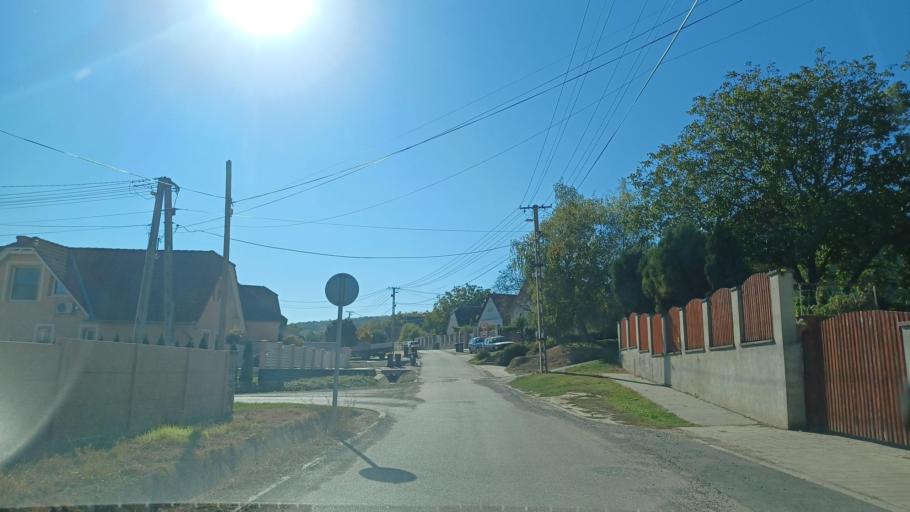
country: HU
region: Tolna
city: Szekszard
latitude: 46.3137
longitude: 18.6927
